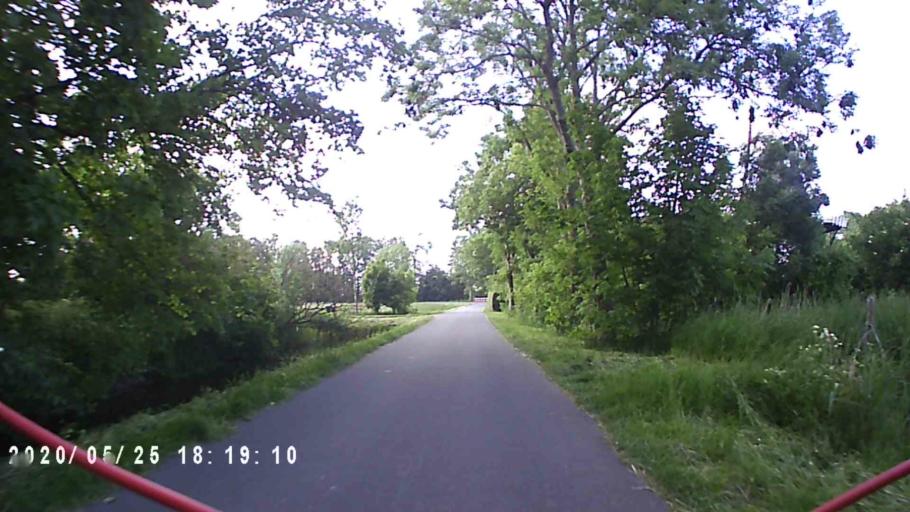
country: NL
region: Groningen
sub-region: Gemeente Zuidhorn
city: Aduard
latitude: 53.3047
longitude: 6.4647
